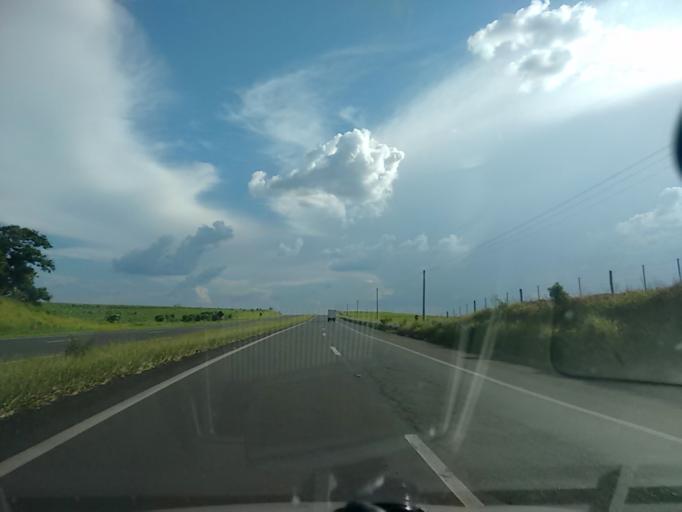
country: BR
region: Sao Paulo
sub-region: Duartina
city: Duartina
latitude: -22.2875
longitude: -49.4923
